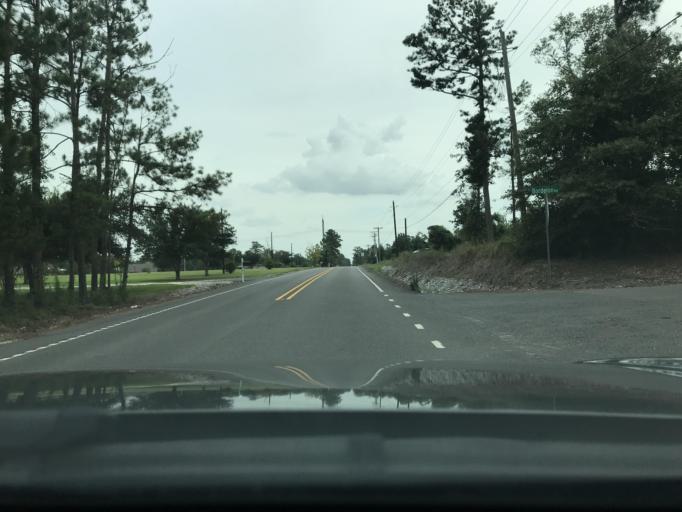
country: US
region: Louisiana
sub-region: Calcasieu Parish
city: Moss Bluff
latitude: 30.3343
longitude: -93.2580
